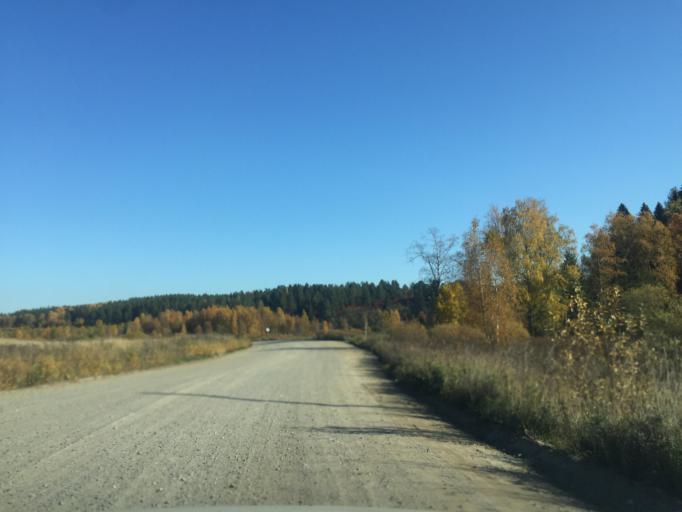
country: RU
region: Leningrad
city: Kuznechnoye
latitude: 61.3090
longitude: 29.9332
